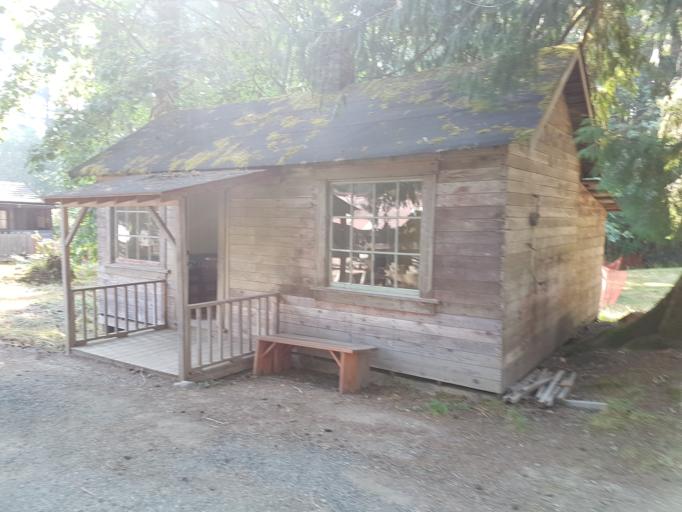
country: CA
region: British Columbia
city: Port Alberni
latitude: 49.3103
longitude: -124.8275
